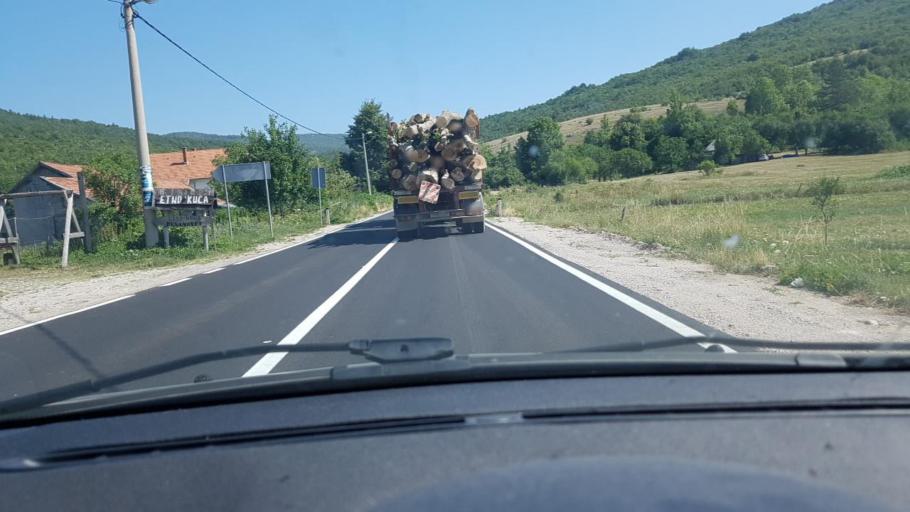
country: BA
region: Federation of Bosnia and Herzegovina
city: Bosansko Grahovo
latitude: 44.2956
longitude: 16.3037
